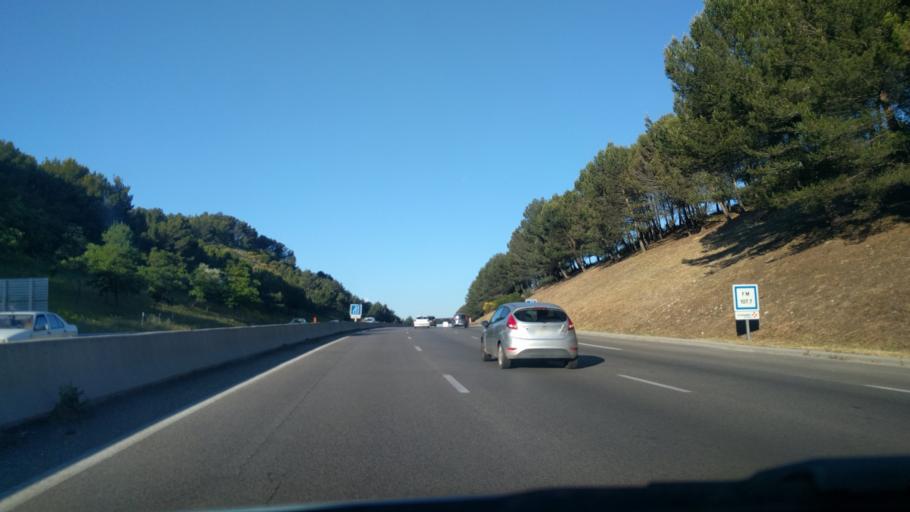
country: FR
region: Provence-Alpes-Cote d'Azur
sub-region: Departement des Bouches-du-Rhone
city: Venelles
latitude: 43.6000
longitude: 5.4943
